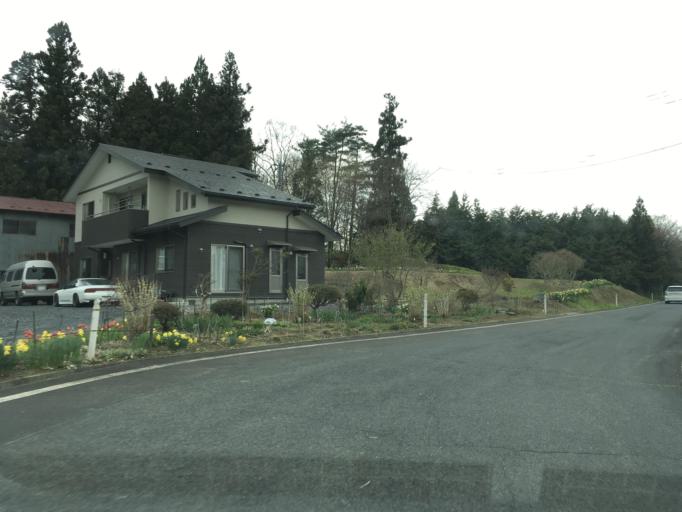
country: JP
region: Iwate
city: Ichinoseki
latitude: 38.8467
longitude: 141.3318
